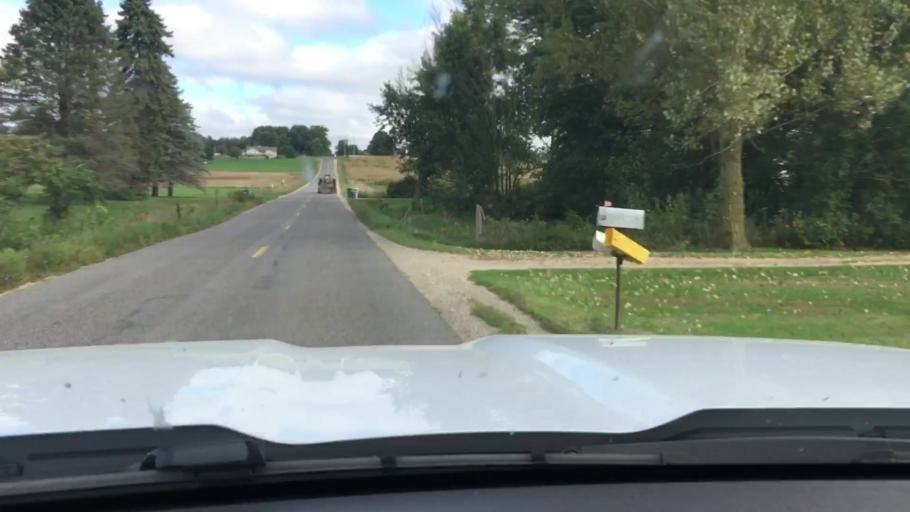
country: US
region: Michigan
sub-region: Kent County
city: Byron Center
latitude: 42.7923
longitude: -85.8026
